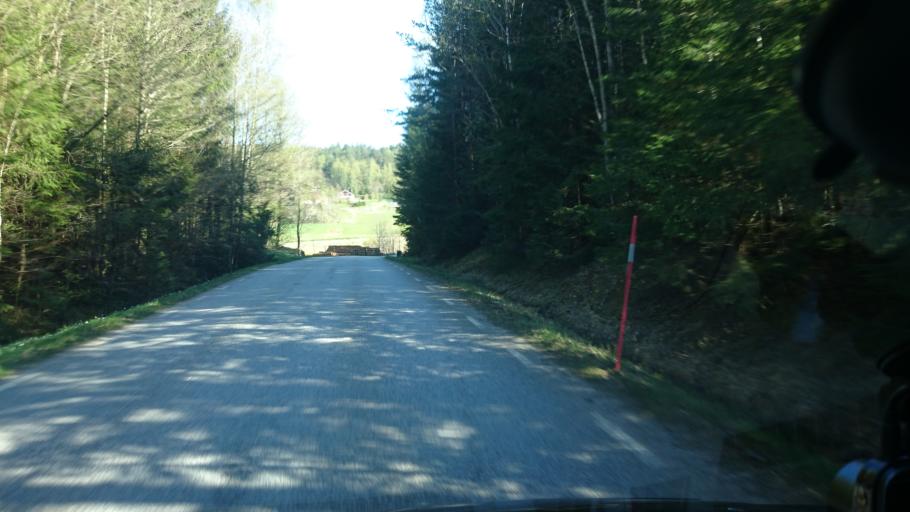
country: SE
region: Vaestra Goetaland
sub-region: Munkedals Kommun
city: Munkedal
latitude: 58.4109
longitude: 11.6734
